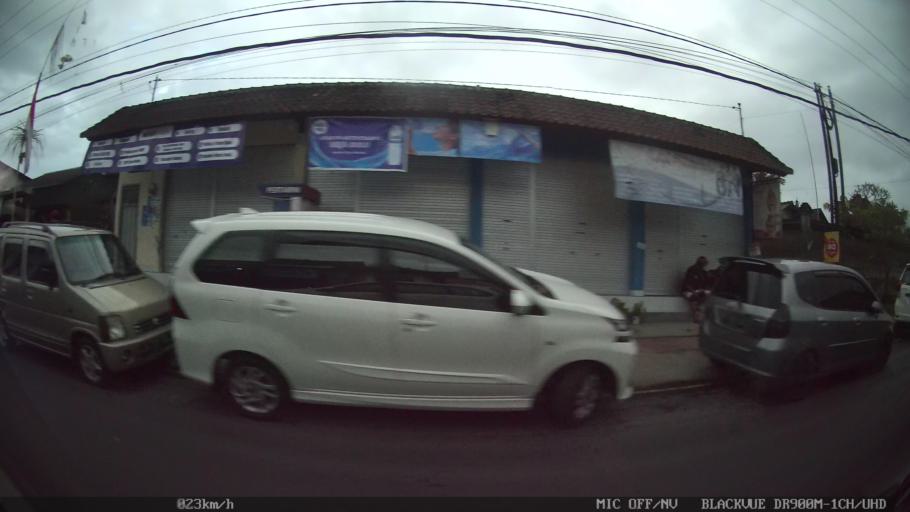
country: ID
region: Bali
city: Banjar Pasekan
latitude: -8.6160
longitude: 115.2838
